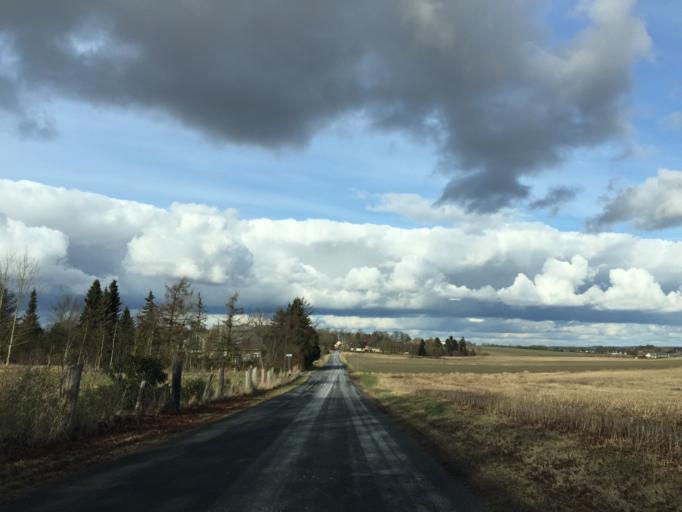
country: DK
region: Central Jutland
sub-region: Favrskov Kommune
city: Hammel
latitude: 56.2009
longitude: 9.8108
